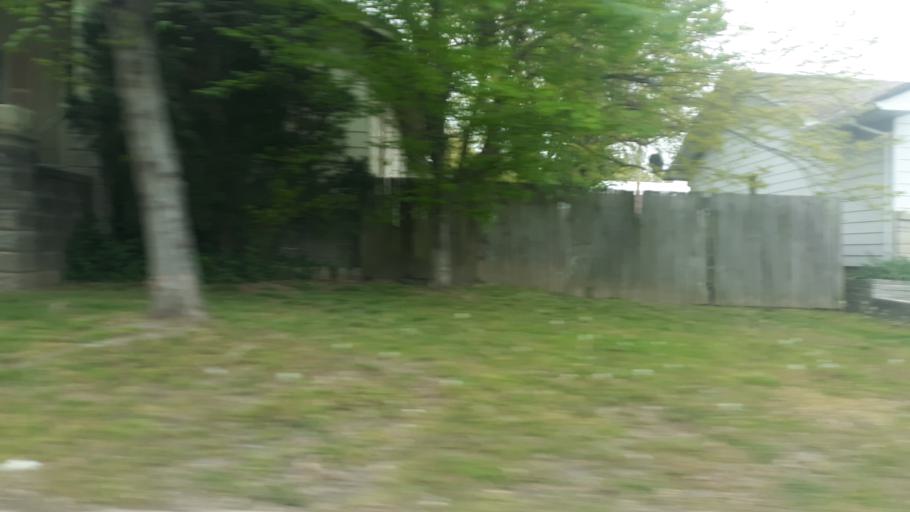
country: US
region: Illinois
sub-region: Williamson County
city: Marion
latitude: 37.7392
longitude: -88.9326
